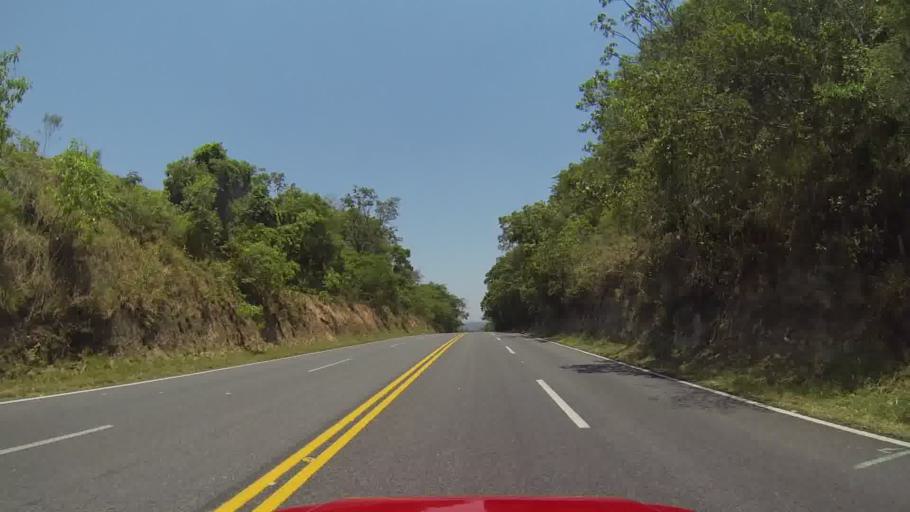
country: BR
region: Minas Gerais
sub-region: Itapecerica
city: Itapecerica
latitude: -20.2909
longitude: -45.1569
